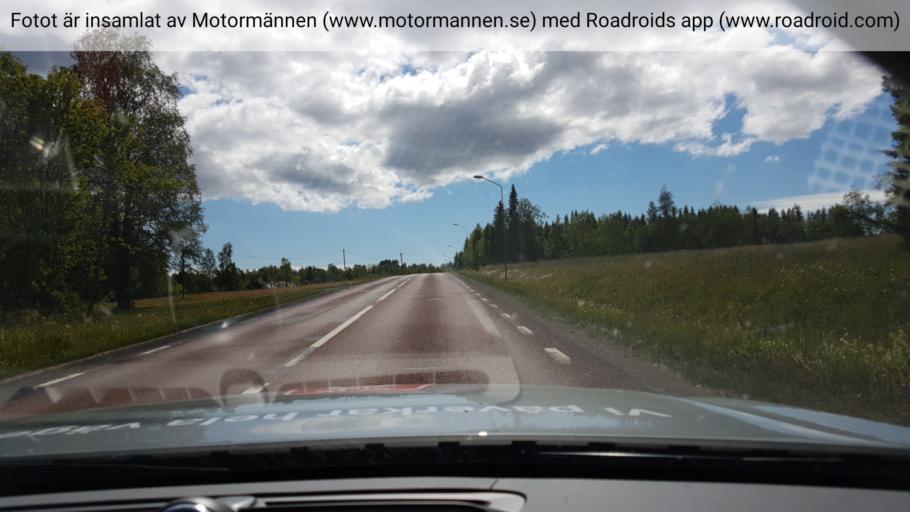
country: SE
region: Jaemtland
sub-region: Stroemsunds Kommun
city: Stroemsund
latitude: 63.7412
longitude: 15.4886
